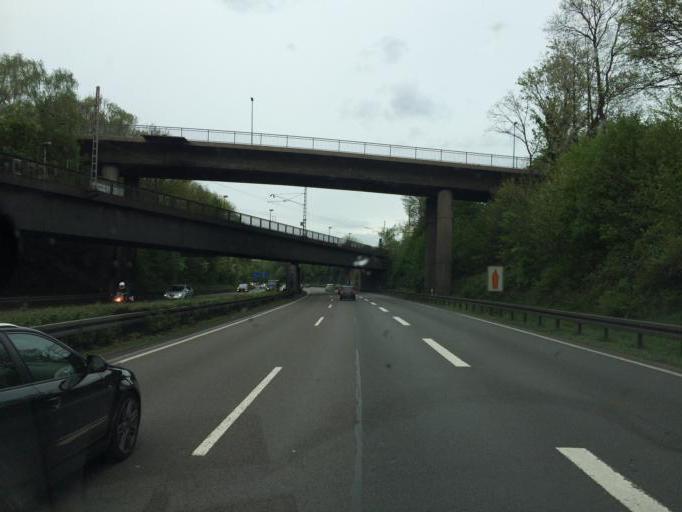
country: DE
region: North Rhine-Westphalia
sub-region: Regierungsbezirk Arnsberg
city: Herne
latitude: 51.5361
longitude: 7.2069
